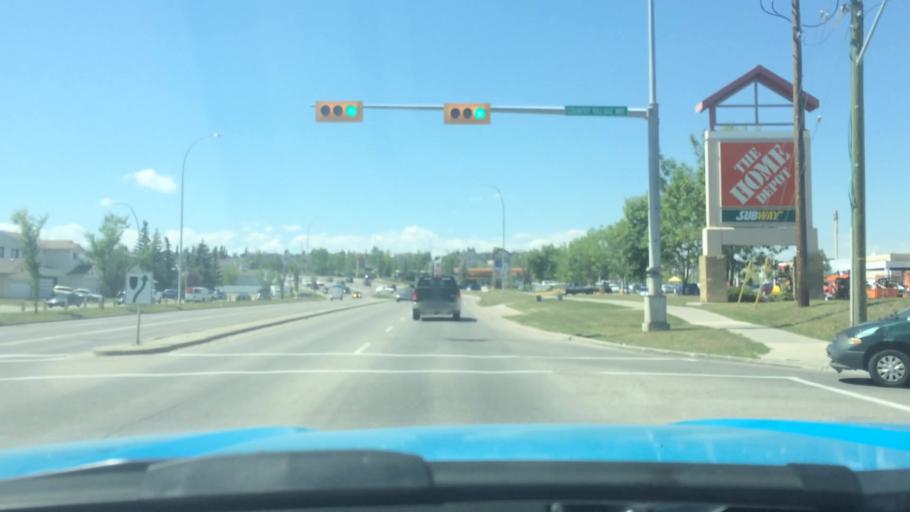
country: CA
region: Alberta
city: Calgary
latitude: 51.1543
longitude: -114.0609
